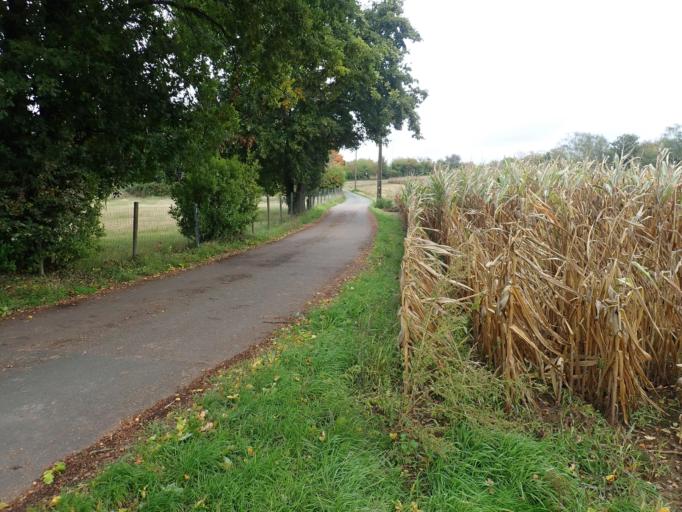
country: BE
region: Flanders
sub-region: Provincie Vlaams-Brabant
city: Aarschot
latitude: 50.9556
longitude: 4.8072
